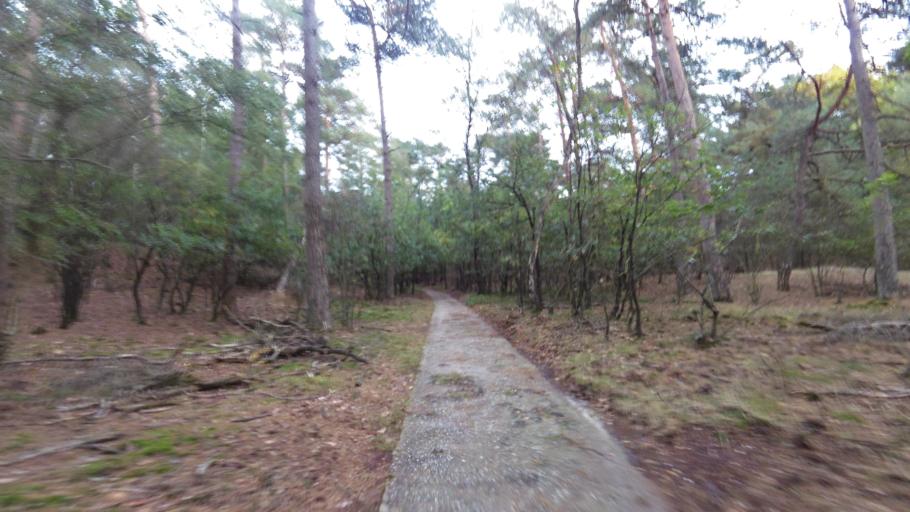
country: NL
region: Gelderland
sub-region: Gemeente Ede
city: Harskamp
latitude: 52.1744
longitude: 5.8295
